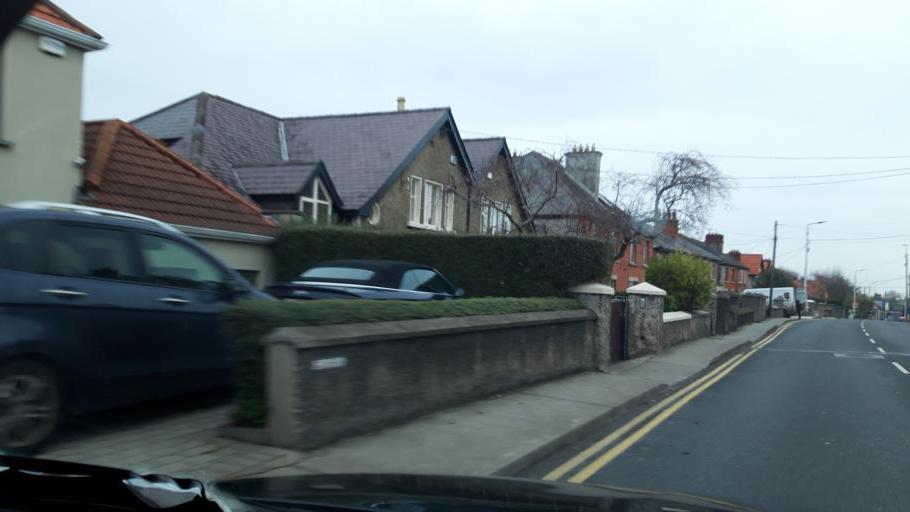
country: IE
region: Leinster
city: Dundrum
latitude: 53.2989
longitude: -6.2465
